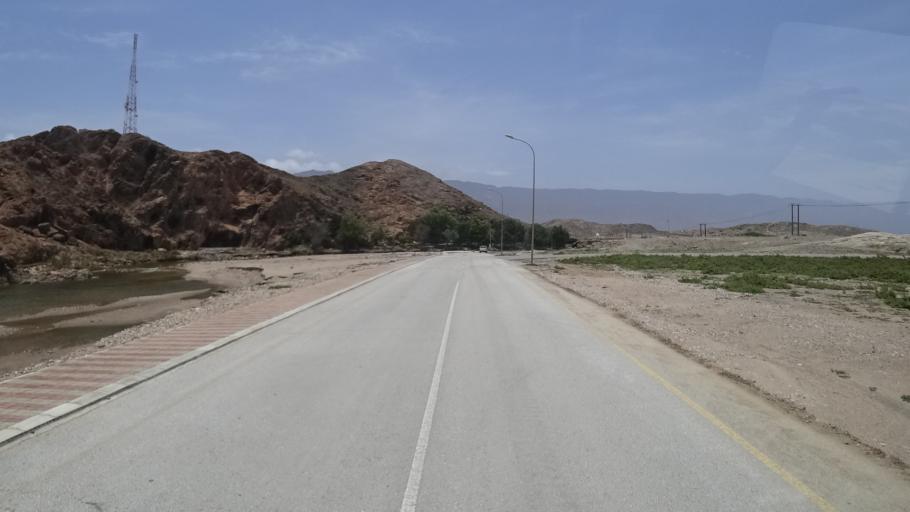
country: OM
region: Zufar
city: Salalah
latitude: 16.9987
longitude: 54.6916
